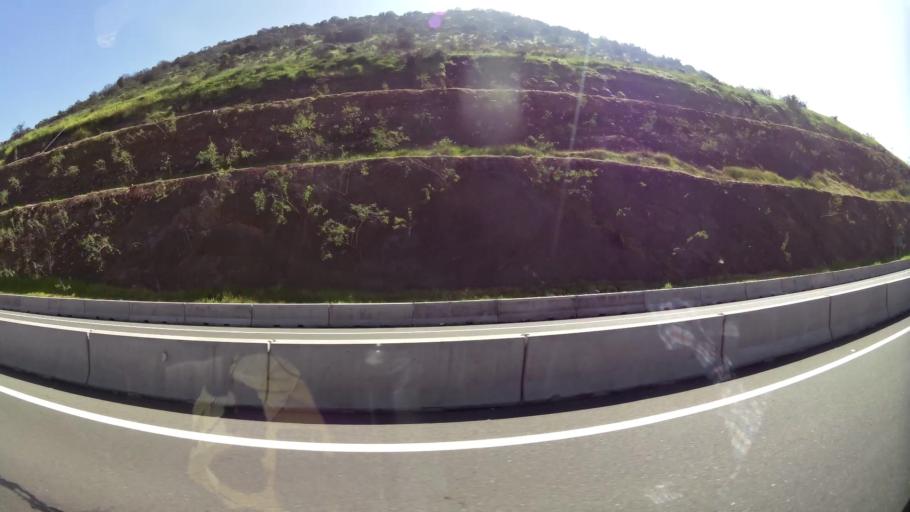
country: CL
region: Santiago Metropolitan
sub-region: Provincia de Chacabuco
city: Chicureo Abajo
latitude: -33.3126
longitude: -70.6485
